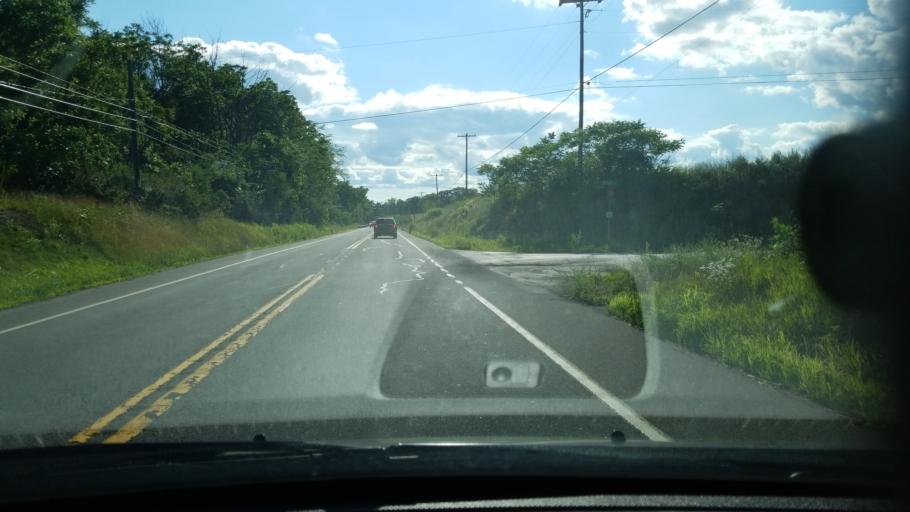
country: US
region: Pennsylvania
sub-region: Northumberland County
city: Elysburg
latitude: 40.8720
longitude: -76.5339
